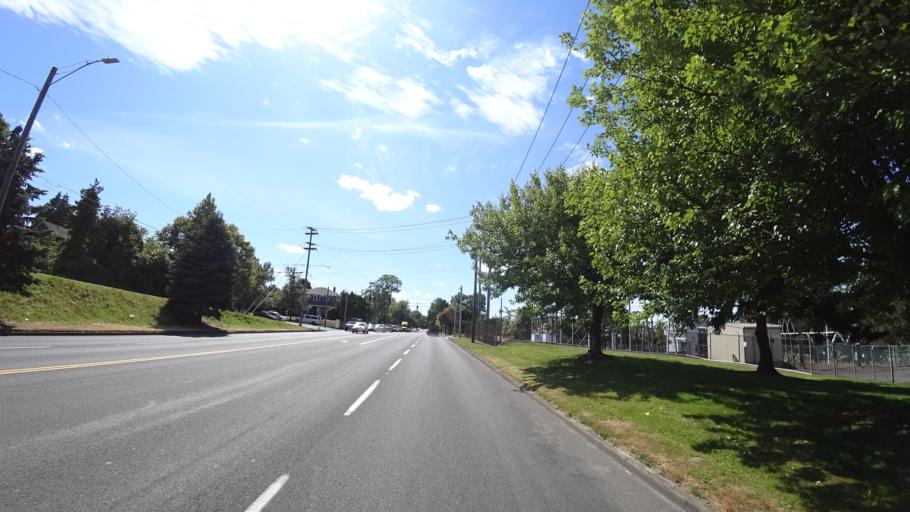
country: US
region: Washington
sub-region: Clark County
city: Vancouver
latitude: 45.5942
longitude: -122.7201
